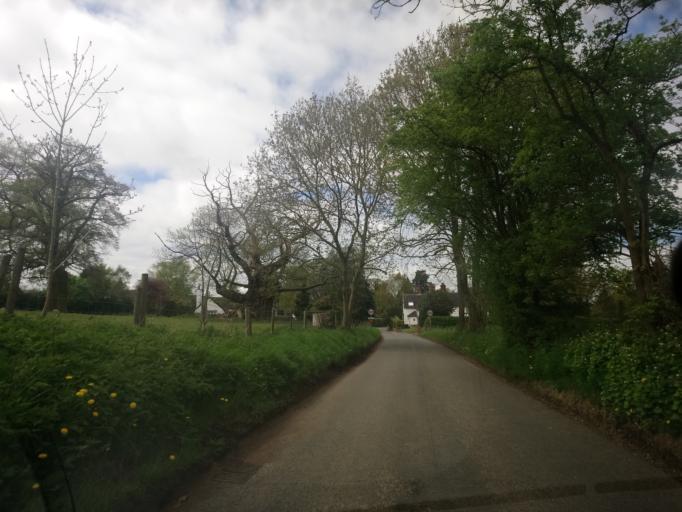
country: GB
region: England
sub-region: Shropshire
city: Prees
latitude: 52.8546
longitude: -2.6436
